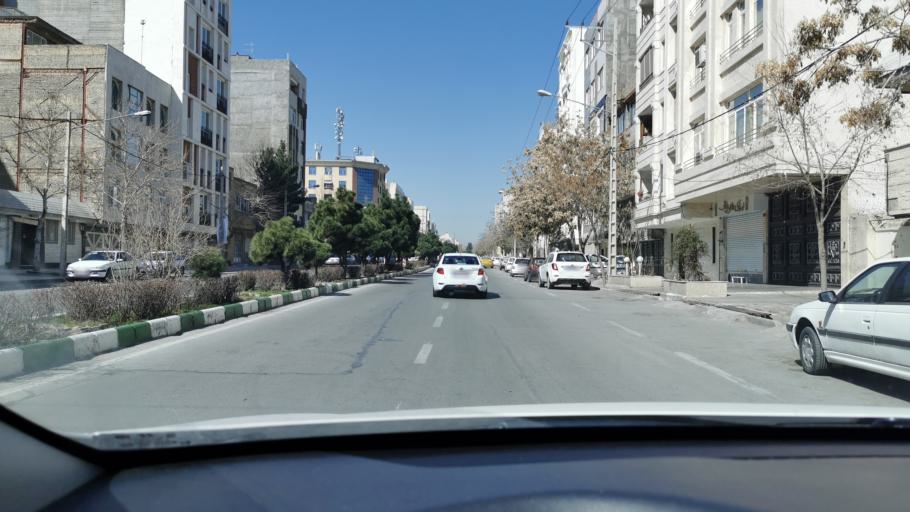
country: IR
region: Razavi Khorasan
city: Mashhad
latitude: 36.3250
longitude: 59.5249
